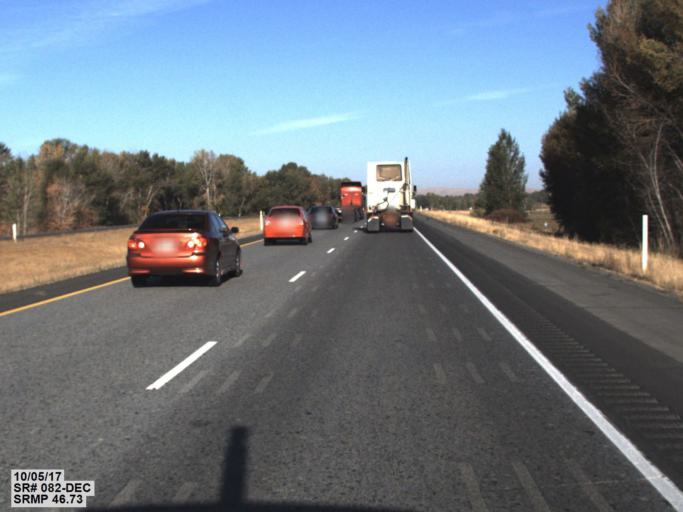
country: US
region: Washington
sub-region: Yakima County
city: Wapato
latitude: 46.4496
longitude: -120.3573
